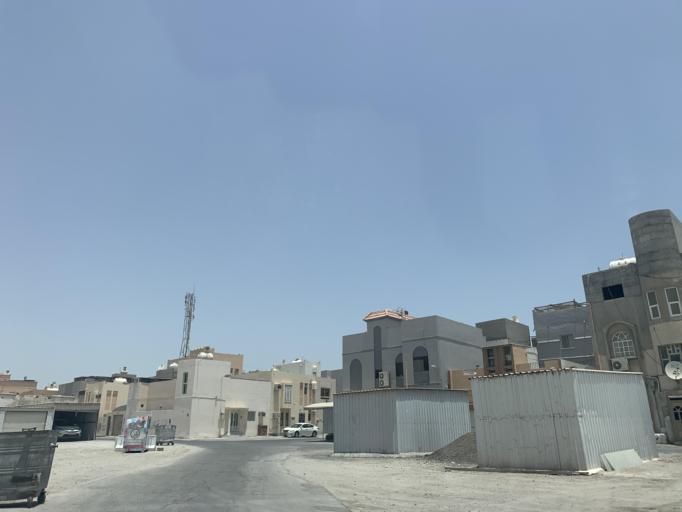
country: BH
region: Northern
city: Sitrah
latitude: 26.1624
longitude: 50.6252
